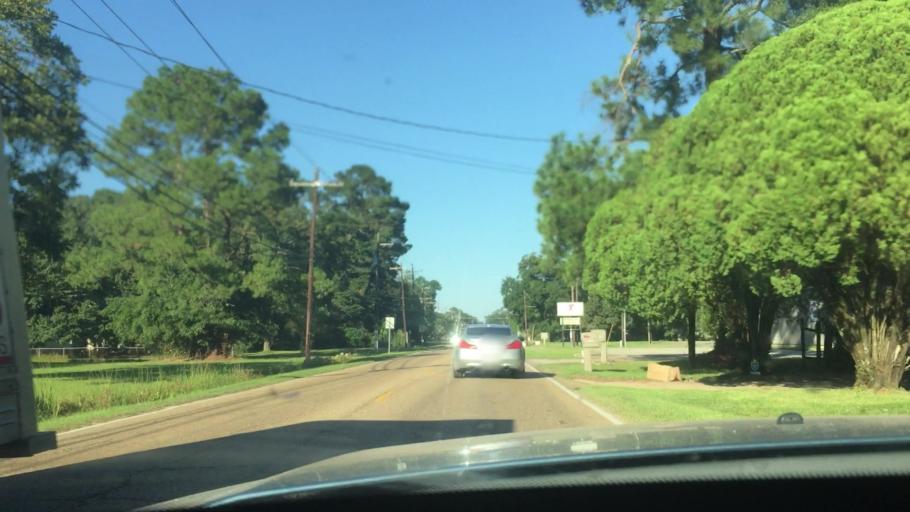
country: US
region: Louisiana
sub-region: East Baton Rouge Parish
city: Monticello
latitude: 30.4578
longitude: -91.0129
